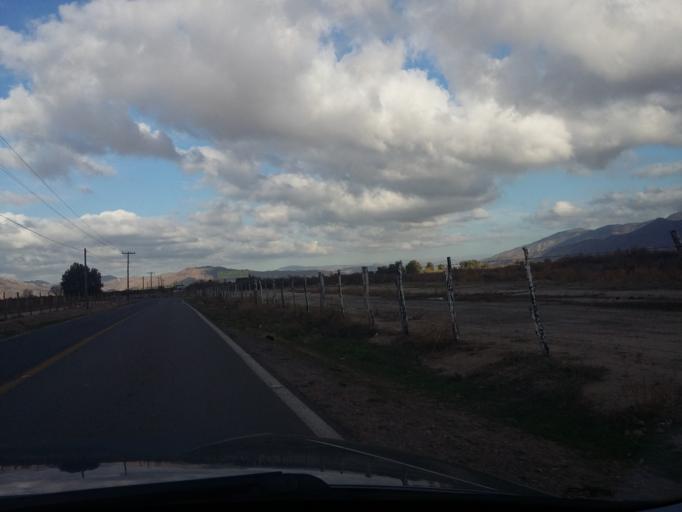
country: MX
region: Baja California
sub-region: Ensenada
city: Rancho Verde
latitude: 32.0617
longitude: -116.6450
